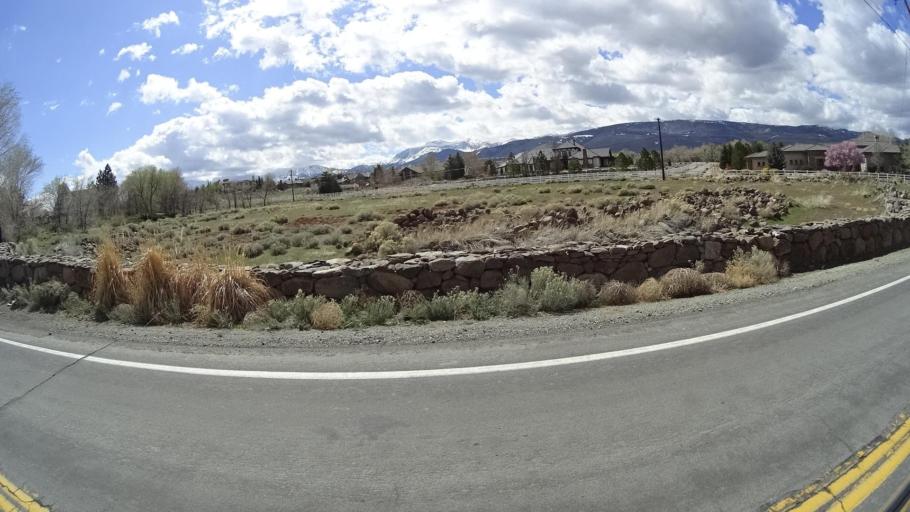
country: US
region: Nevada
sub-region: Washoe County
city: Reno
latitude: 39.4284
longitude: -119.7859
